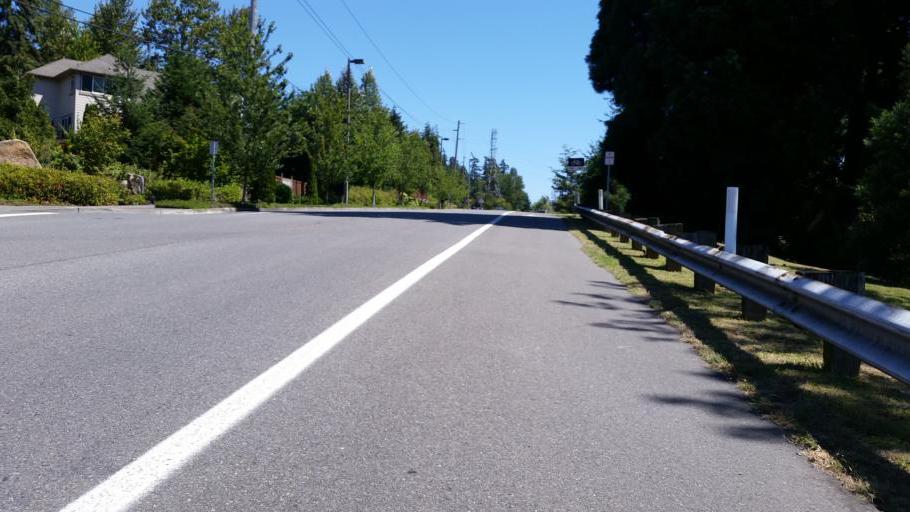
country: US
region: Washington
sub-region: King County
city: Bellevue
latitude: 47.6326
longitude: -122.1798
